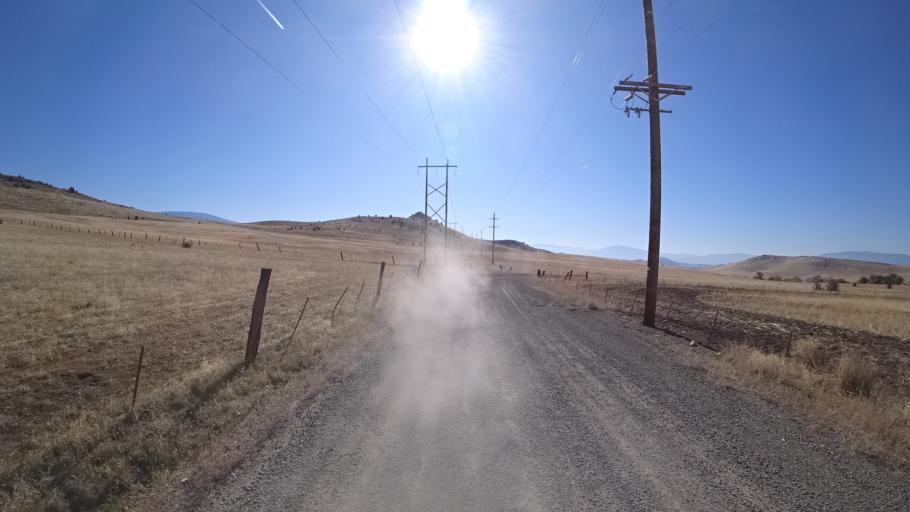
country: US
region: California
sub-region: Siskiyou County
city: Montague
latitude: 41.7500
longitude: -122.3596
